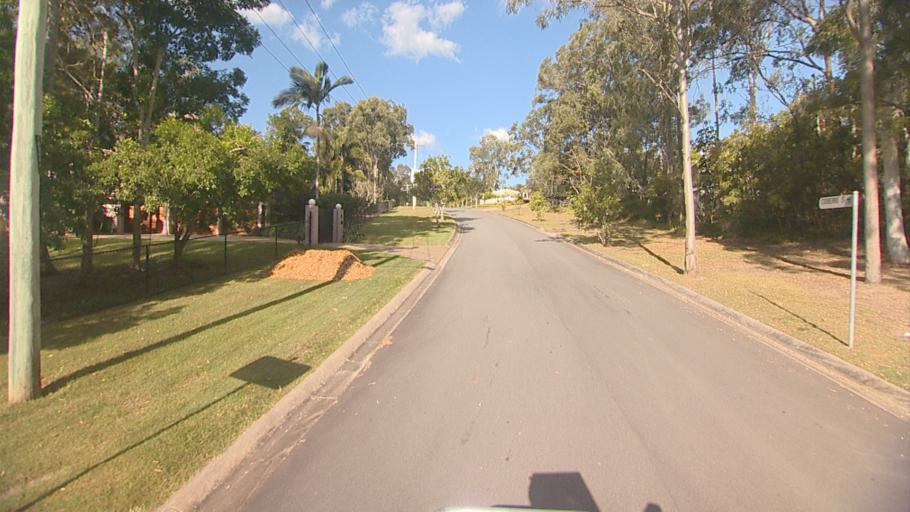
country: AU
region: Queensland
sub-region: Logan
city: Beenleigh
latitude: -27.6696
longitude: 153.2167
